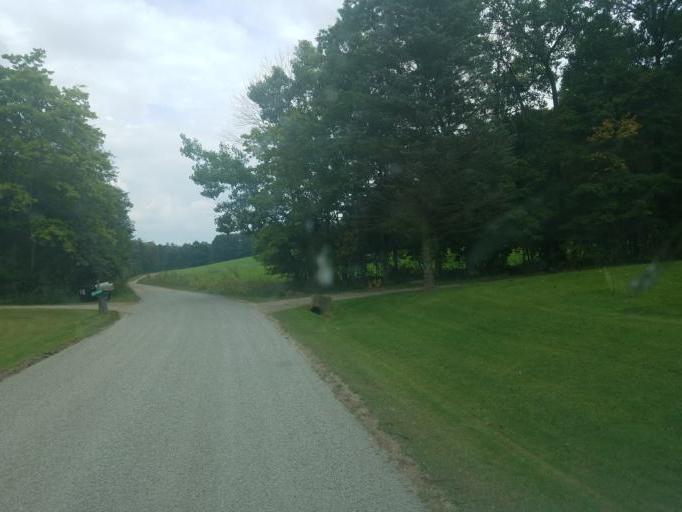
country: US
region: Ohio
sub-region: Knox County
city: Danville
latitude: 40.4756
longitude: -82.3216
